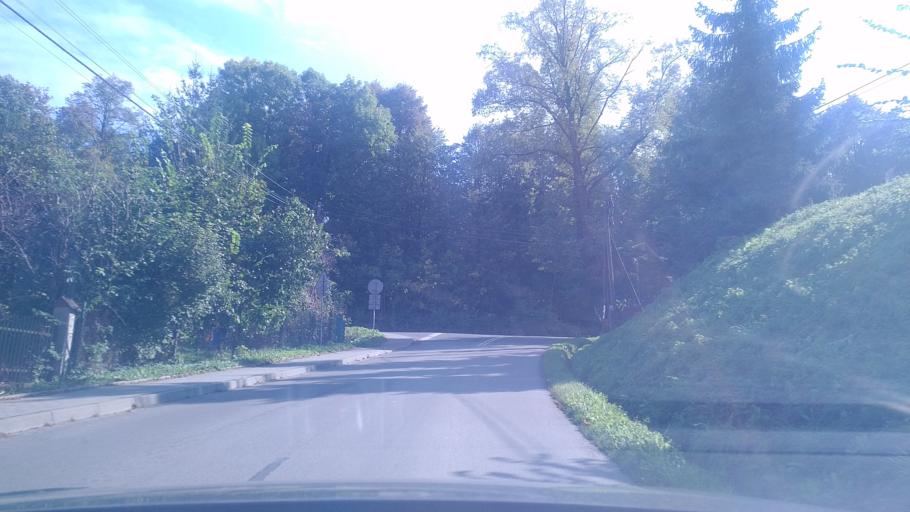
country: PL
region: Lesser Poland Voivodeship
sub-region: Powiat krakowski
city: Modlnica
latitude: 50.1319
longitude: 19.8623
